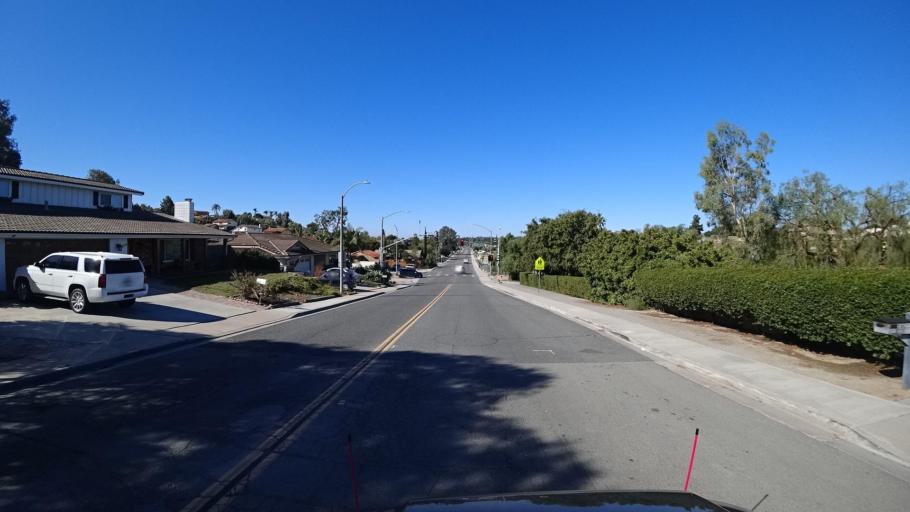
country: US
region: California
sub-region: San Diego County
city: Bonita
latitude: 32.6721
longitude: -117.0110
